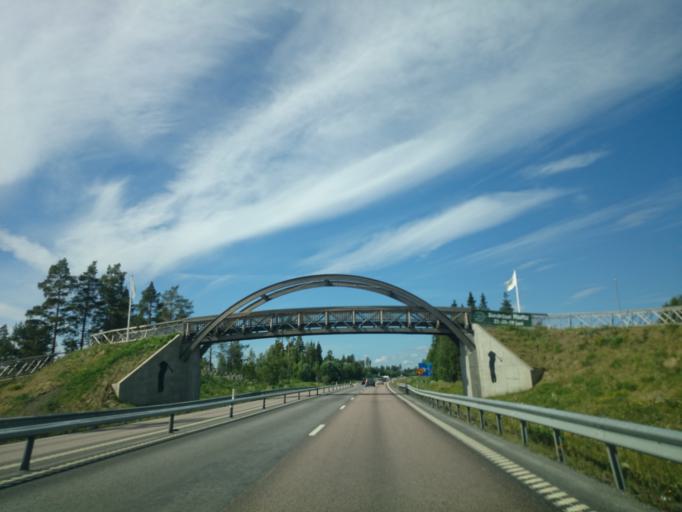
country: SE
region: Jaemtland
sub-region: Krokoms Kommun
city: Krokom
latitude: 63.2890
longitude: 14.5093
